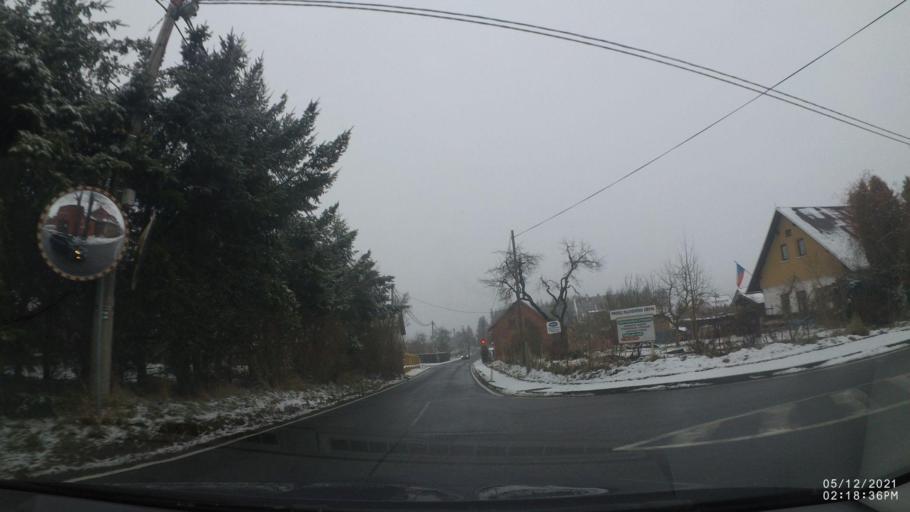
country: CZ
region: Kralovehradecky
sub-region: Okres Nachod
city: Cerveny Kostelec
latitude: 50.4539
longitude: 16.1339
